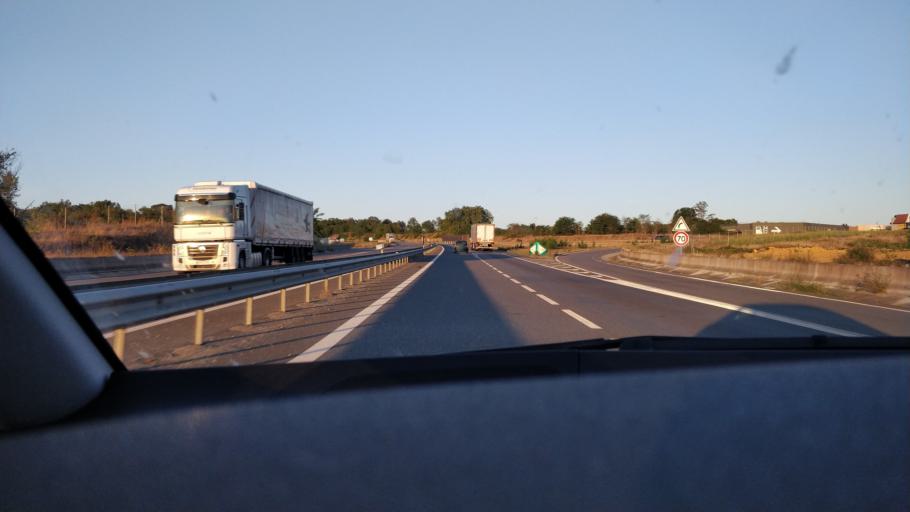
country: FR
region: Poitou-Charentes
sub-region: Departement de la Charente
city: La Rochefoucauld
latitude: 45.7532
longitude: 0.3805
